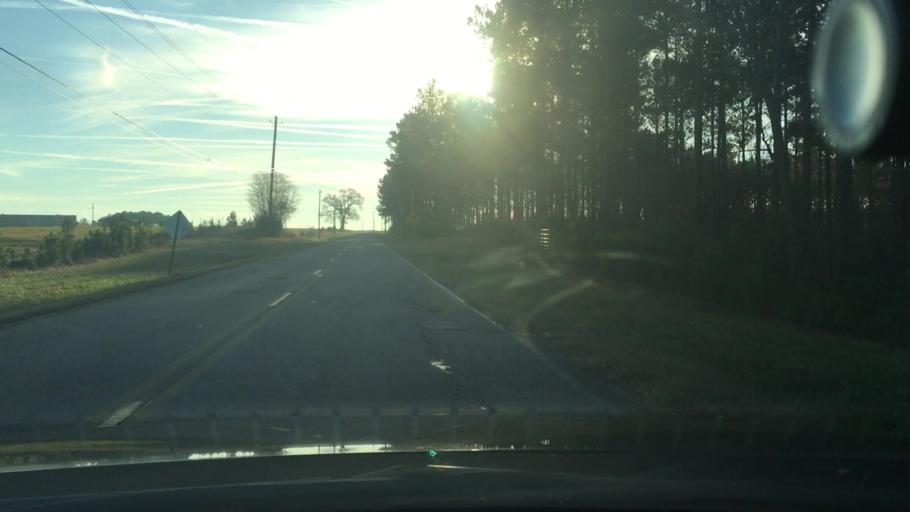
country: US
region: Georgia
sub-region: Spalding County
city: Experiment
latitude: 33.2659
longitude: -84.3103
